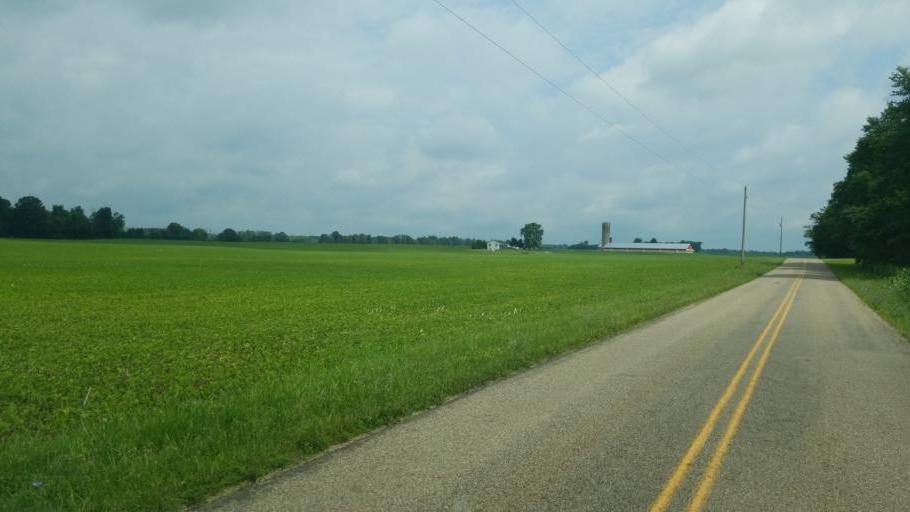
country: US
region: Ohio
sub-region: Knox County
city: Centerburg
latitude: 40.3043
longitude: -82.6246
